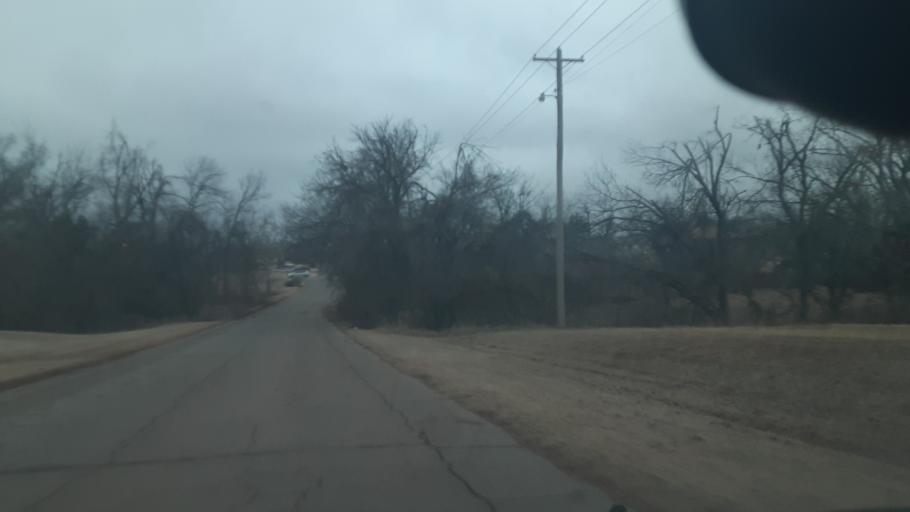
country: US
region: Oklahoma
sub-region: Logan County
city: Guthrie
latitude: 35.8780
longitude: -97.4056
